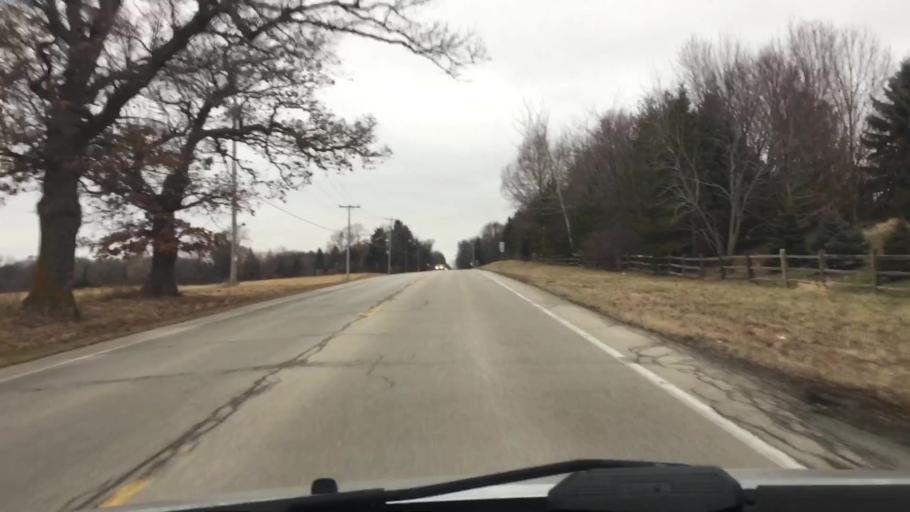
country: US
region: Wisconsin
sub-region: Waukesha County
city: Nashotah
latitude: 43.0882
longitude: -88.4032
